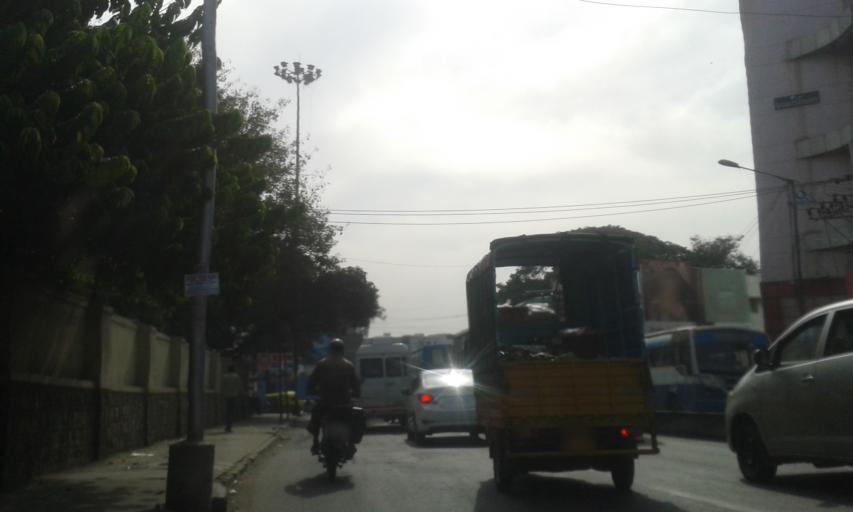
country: IN
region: Karnataka
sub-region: Bangalore Urban
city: Bangalore
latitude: 12.9324
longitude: 77.6130
